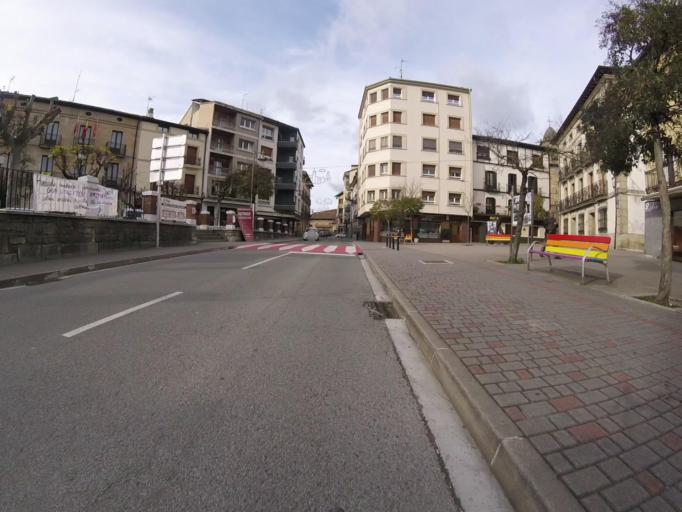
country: ES
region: Navarre
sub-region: Provincia de Navarra
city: Altsasu
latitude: 42.8950
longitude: -2.1683
